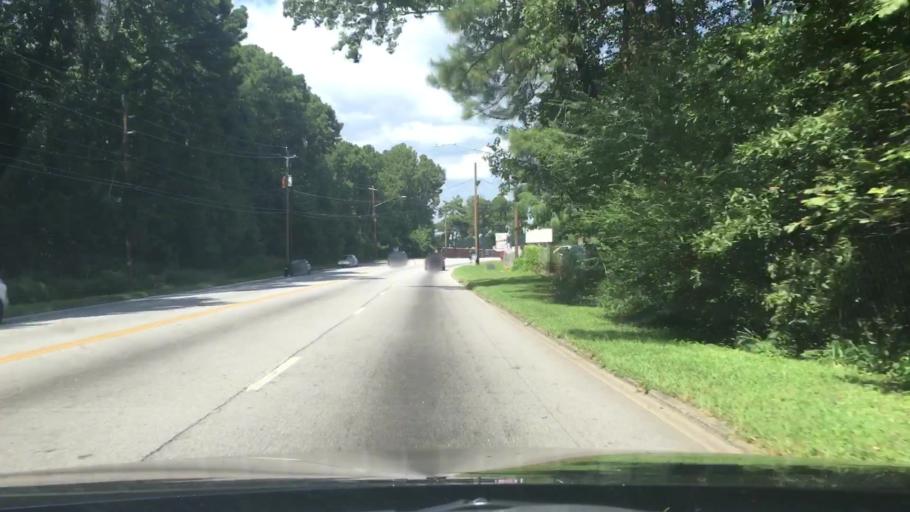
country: US
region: Georgia
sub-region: DeKalb County
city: Lithonia
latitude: 33.7106
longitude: -84.1284
